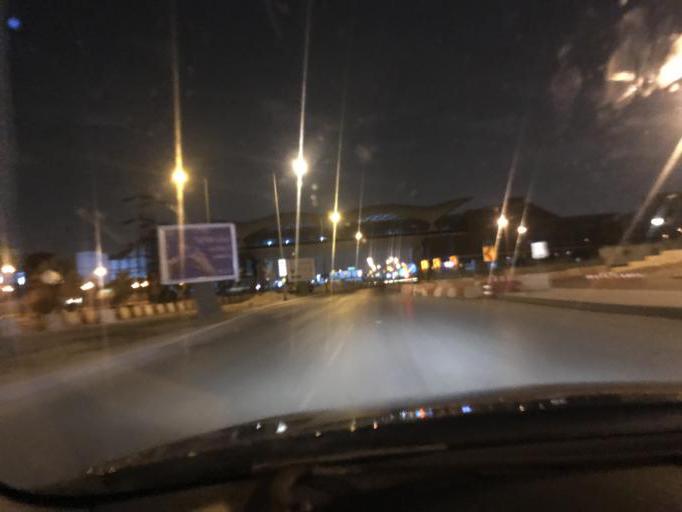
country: SA
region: Ar Riyad
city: Riyadh
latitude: 24.8029
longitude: 46.6952
